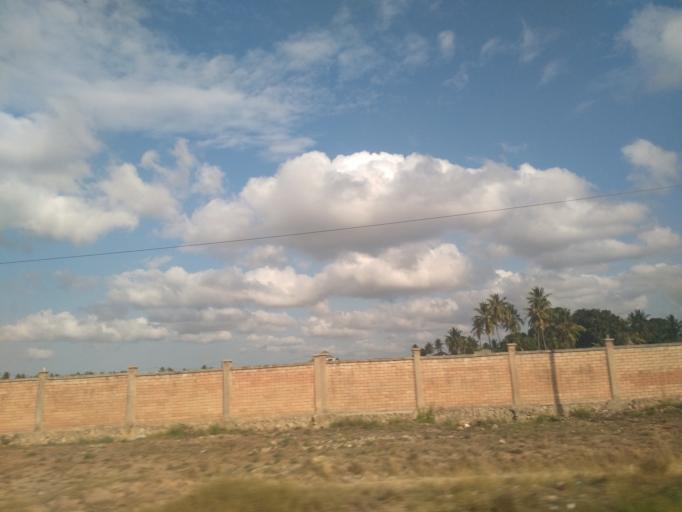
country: TZ
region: Dar es Salaam
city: Dar es Salaam
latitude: -6.8757
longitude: 39.3432
